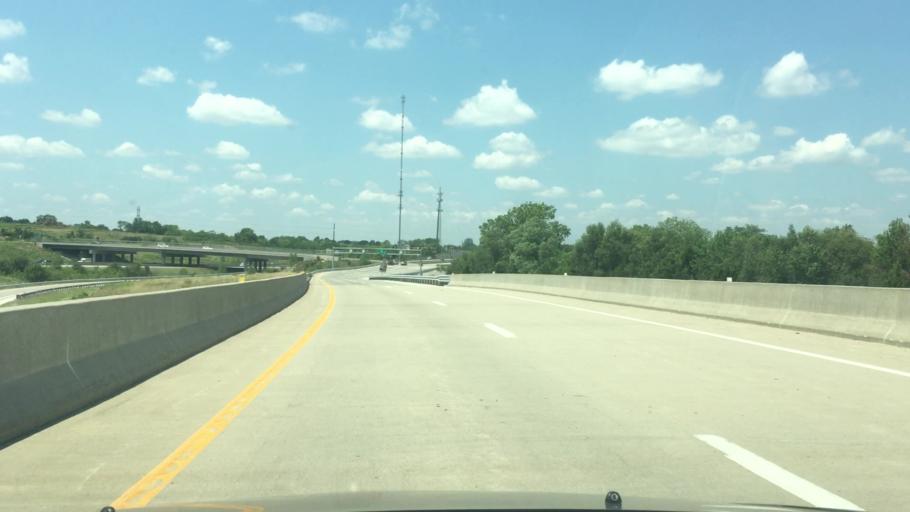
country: US
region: Missouri
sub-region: Jackson County
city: Lees Summit
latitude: 38.9358
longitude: -94.4082
